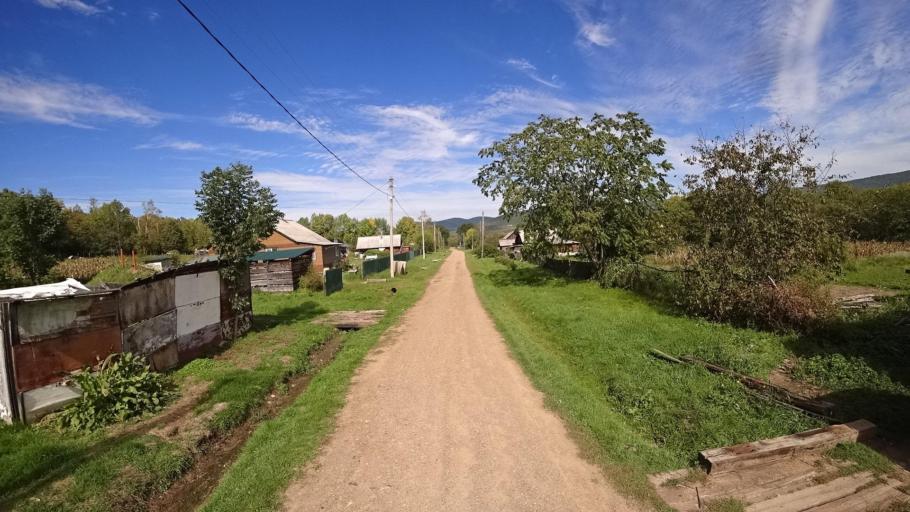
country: RU
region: Primorskiy
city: Yakovlevka
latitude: 44.3937
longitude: 133.5956
